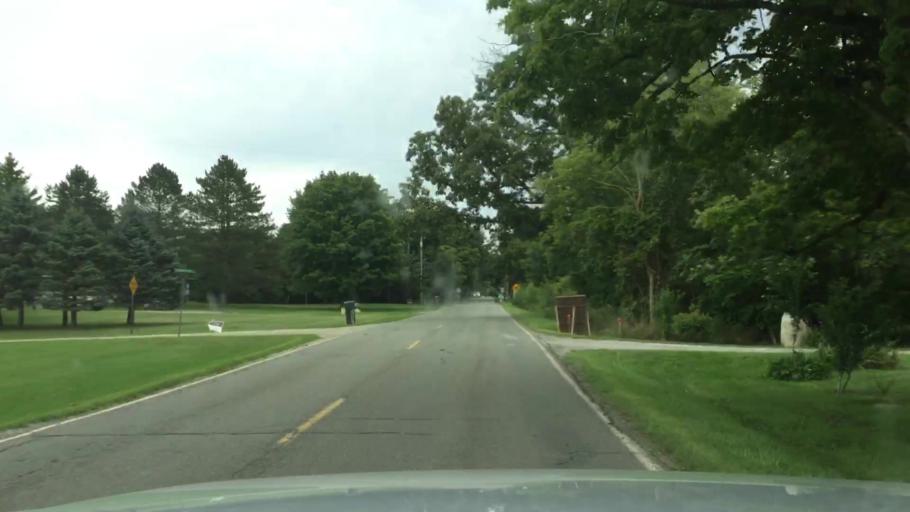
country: US
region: Michigan
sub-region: Shiawassee County
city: Durand
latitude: 42.8238
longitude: -83.9570
